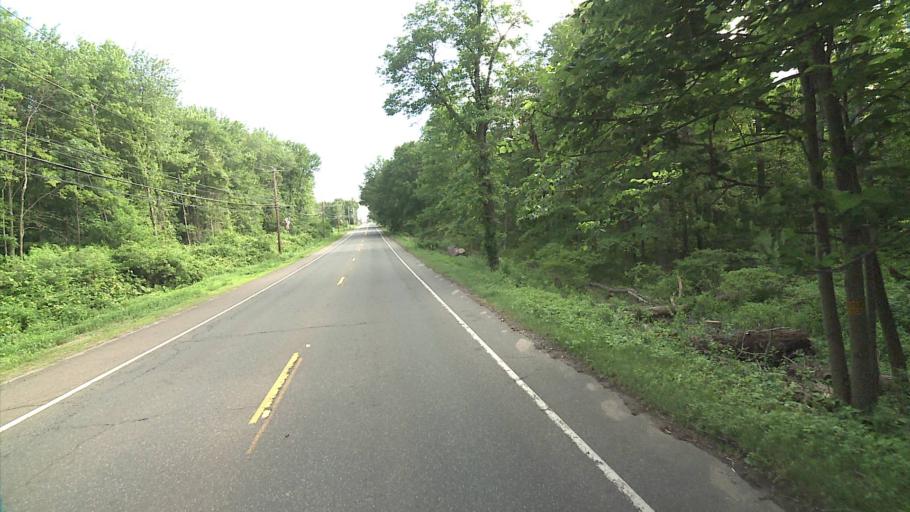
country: US
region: Connecticut
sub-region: New Haven County
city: Prospect
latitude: 41.4305
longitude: -72.9941
